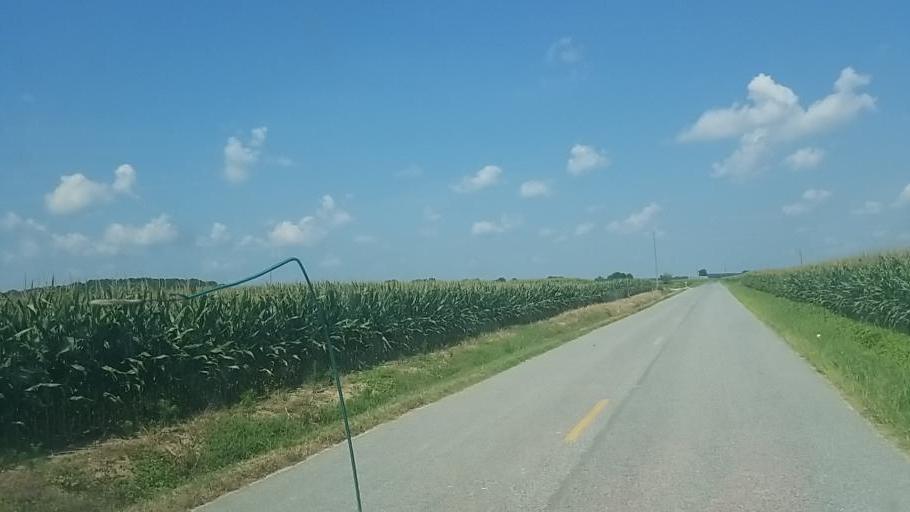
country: US
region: Maryland
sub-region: Worcester County
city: Berlin
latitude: 38.2864
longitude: -75.2364
